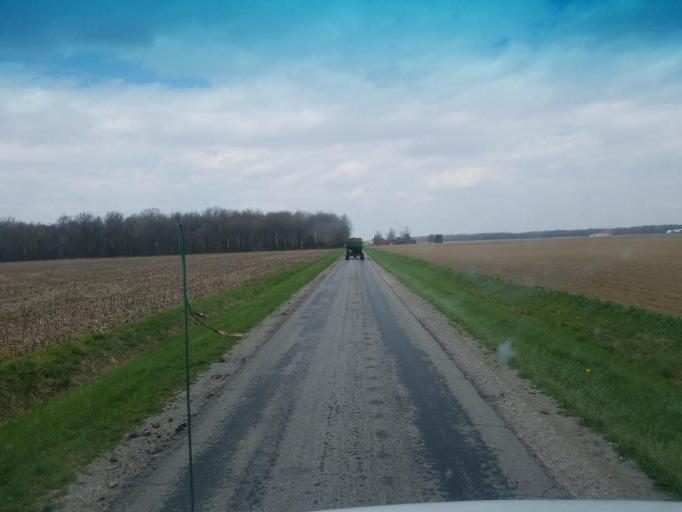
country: US
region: Ohio
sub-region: Crawford County
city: Bucyrus
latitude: 40.9681
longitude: -82.9971
